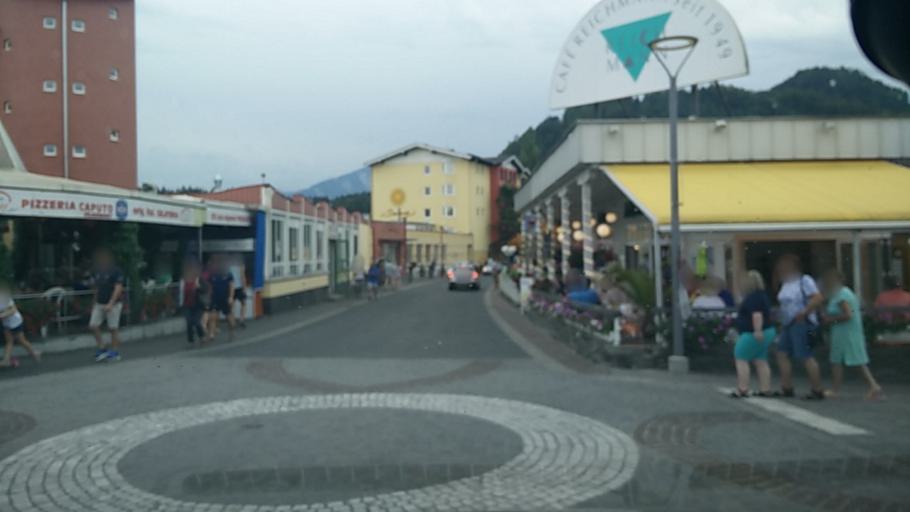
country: AT
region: Carinthia
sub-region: Politischer Bezirk Volkermarkt
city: Sittersdorf
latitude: 46.6070
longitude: 14.5742
